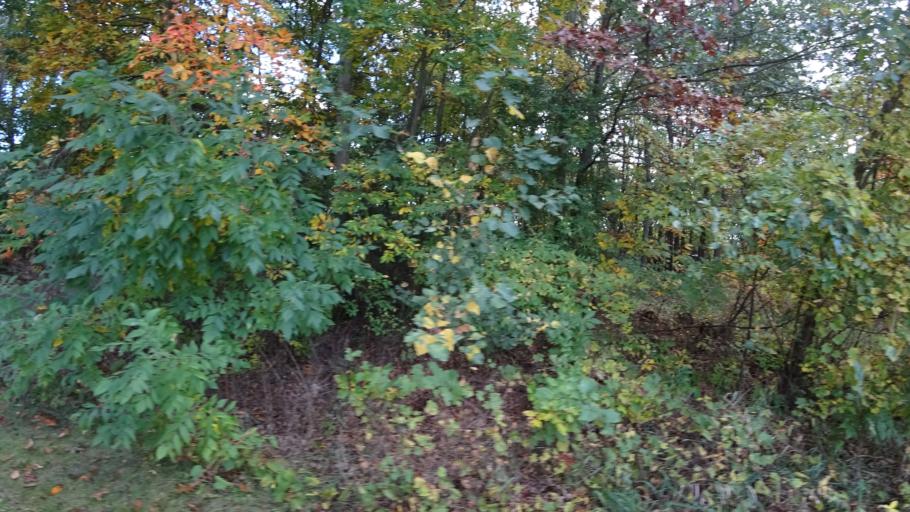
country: US
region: Michigan
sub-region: Saint Joseph County
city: Three Rivers
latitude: 41.9528
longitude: -85.5836
